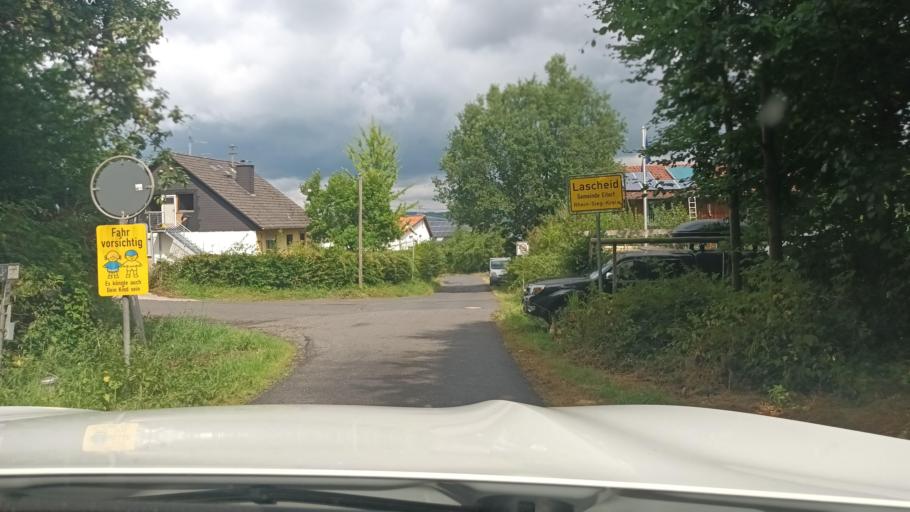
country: DE
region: North Rhine-Westphalia
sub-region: Regierungsbezirk Koln
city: Eitorf
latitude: 50.7509
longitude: 7.4558
